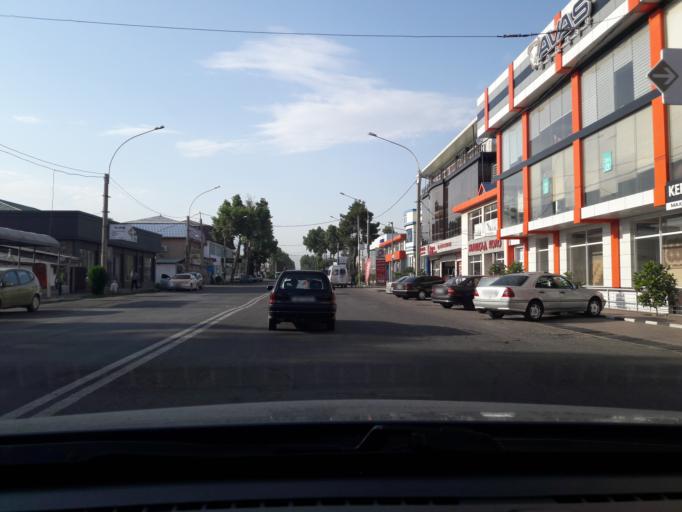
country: TJ
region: Dushanbe
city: Dushanbe
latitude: 38.5508
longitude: 68.7722
